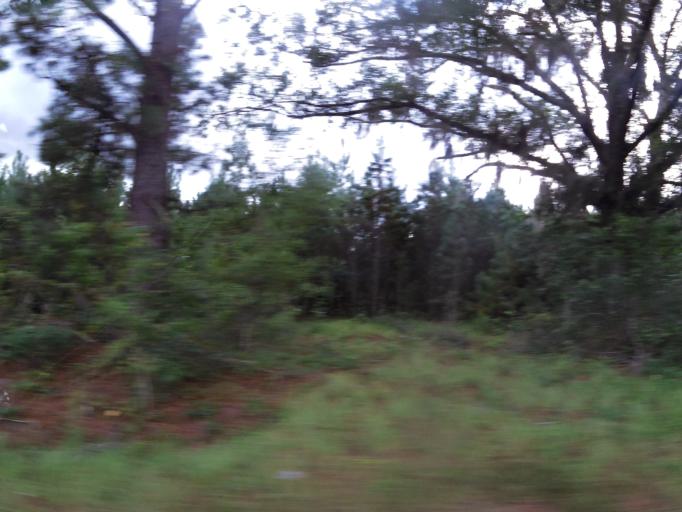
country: US
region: Georgia
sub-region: Liberty County
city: Midway
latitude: 31.8562
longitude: -81.4266
